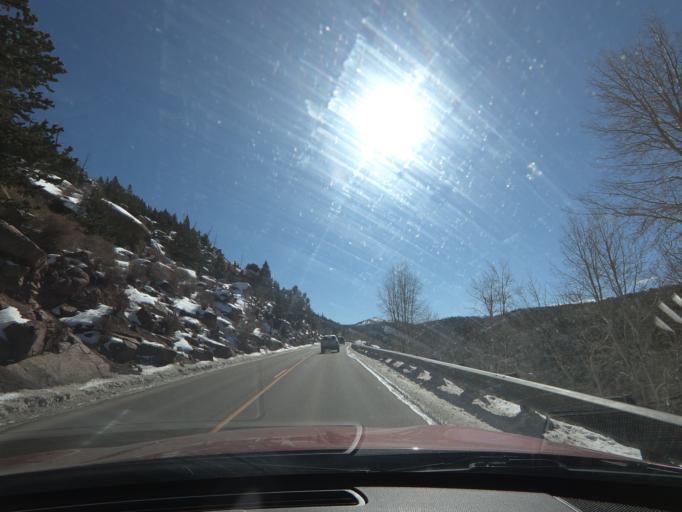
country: US
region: Colorado
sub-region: Teller County
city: Cripple Creek
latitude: 38.8127
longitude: -105.1282
